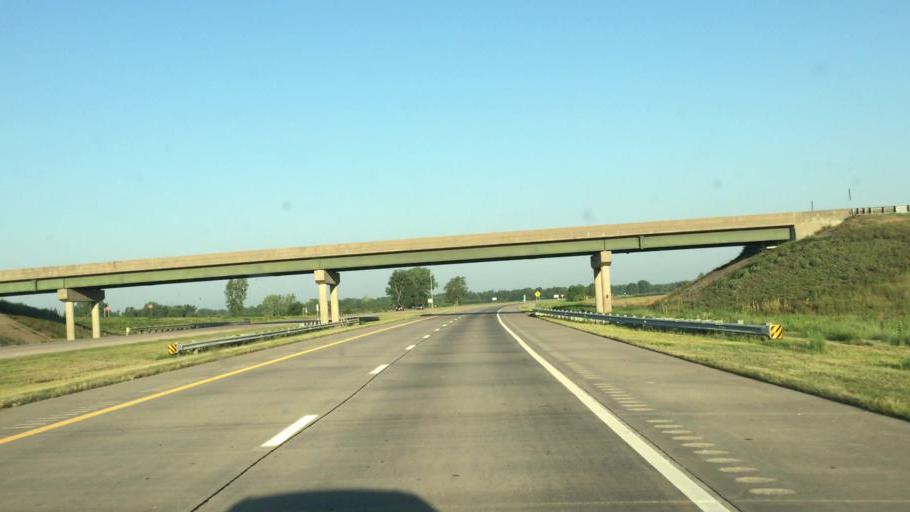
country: US
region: Kansas
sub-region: Doniphan County
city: Elwood
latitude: 39.7413
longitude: -94.8930
